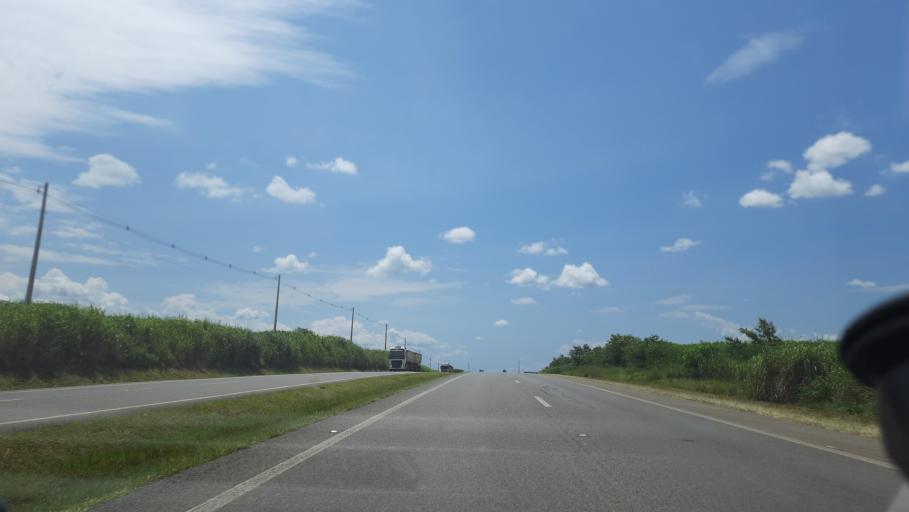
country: BR
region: Sao Paulo
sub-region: Mococa
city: Mococa
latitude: -21.6005
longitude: -47.0410
